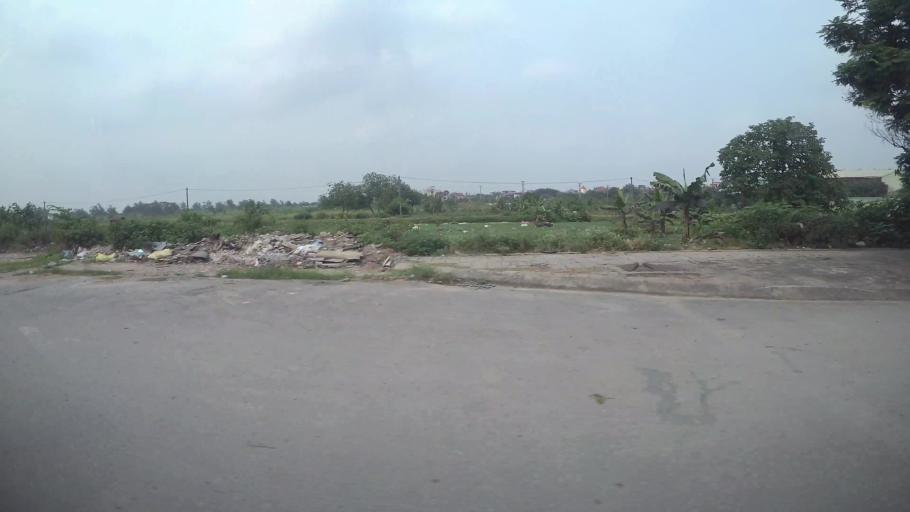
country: VN
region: Ha Noi
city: Hoan Kiem
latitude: 21.0728
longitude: 105.8987
